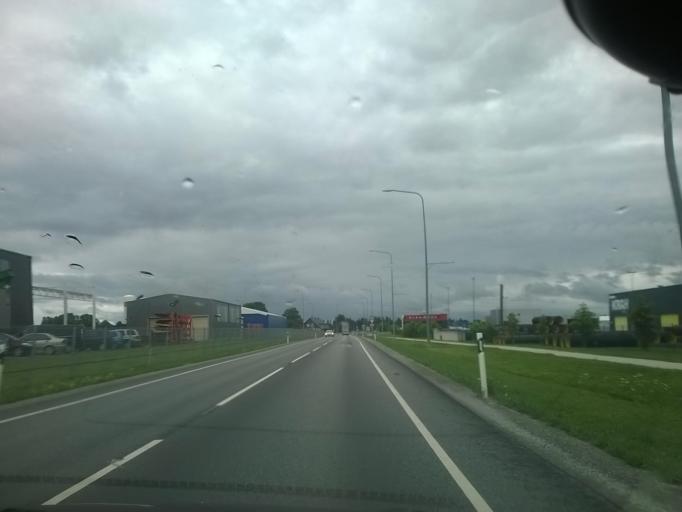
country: EE
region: Harju
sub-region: Rae vald
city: Jueri
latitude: 59.3629
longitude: 24.8779
